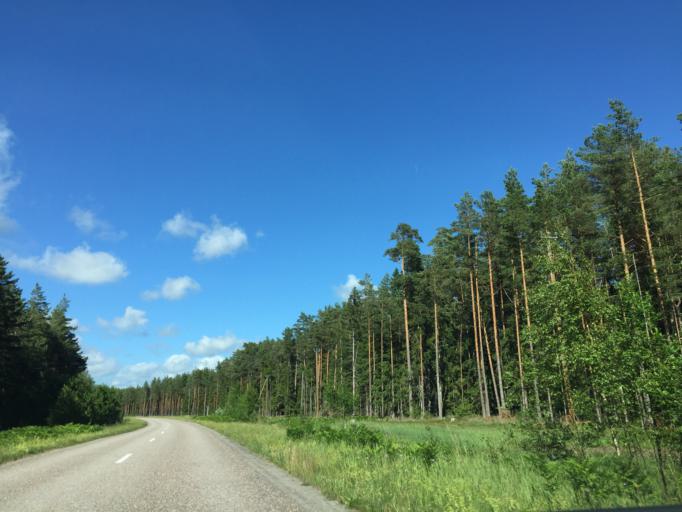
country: LV
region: Ventspils
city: Ventspils
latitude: 57.4956
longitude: 21.6858
